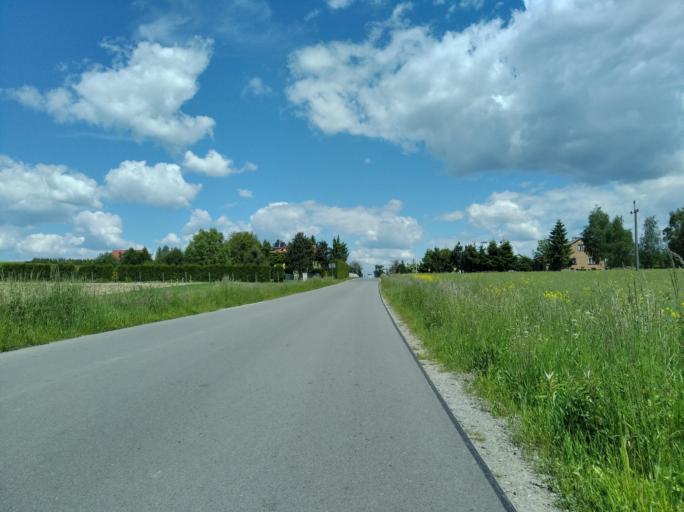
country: PL
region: Subcarpathian Voivodeship
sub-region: Powiat jasielski
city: Tarnowiec
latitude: 49.7745
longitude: 21.6112
